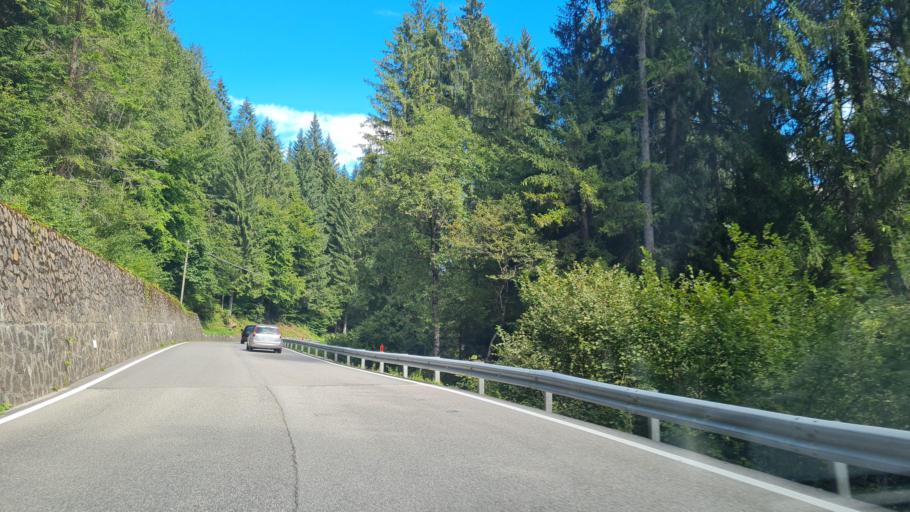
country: IT
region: Trentino-Alto Adige
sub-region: Provincia di Trento
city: Siror
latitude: 46.2185
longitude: 11.8125
